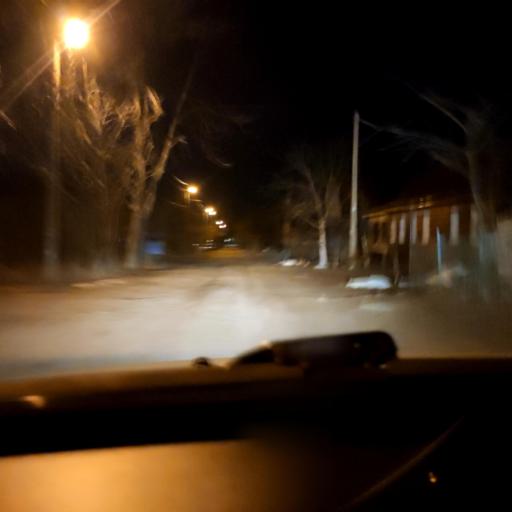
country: RU
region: Voronezj
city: Somovo
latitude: 51.7370
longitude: 39.2779
